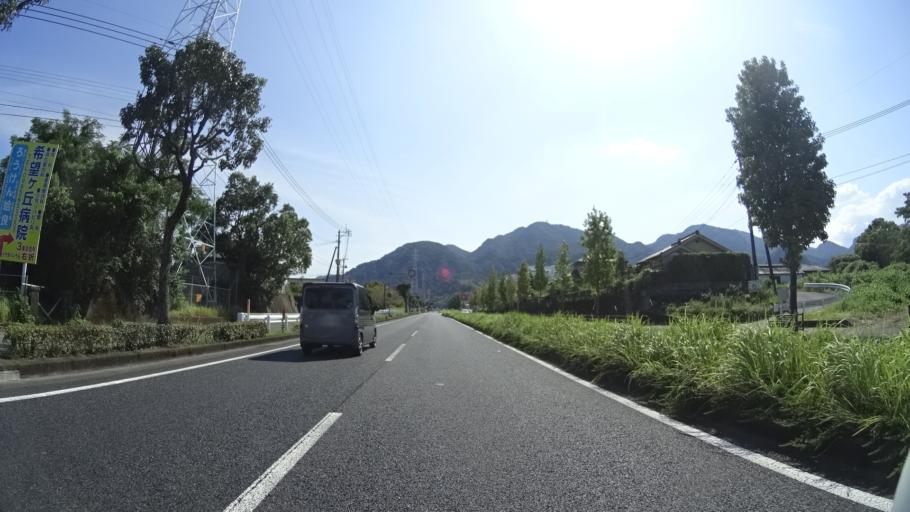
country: JP
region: Kagoshima
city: Kajiki
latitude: 31.7114
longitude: 130.6165
